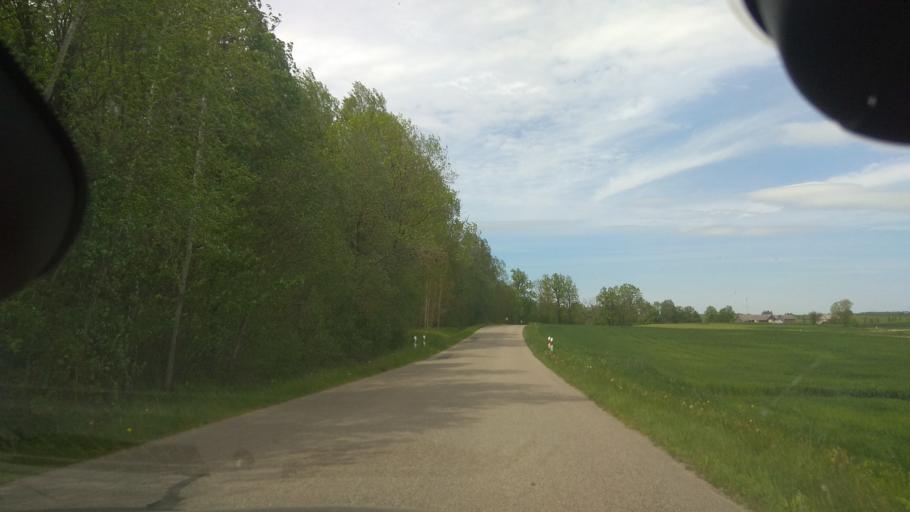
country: LT
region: Vilnius County
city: Ukmerge
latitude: 55.1523
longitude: 24.5472
